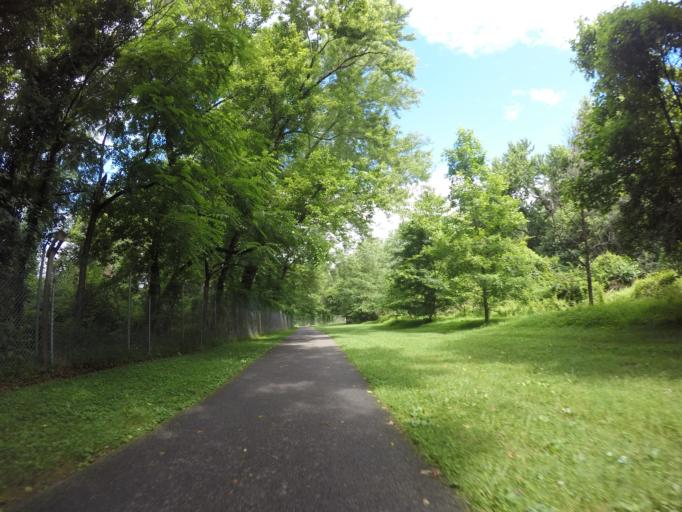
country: US
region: Maryland
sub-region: Prince George's County
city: Berwyn Heights
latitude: 38.9802
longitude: -76.9201
